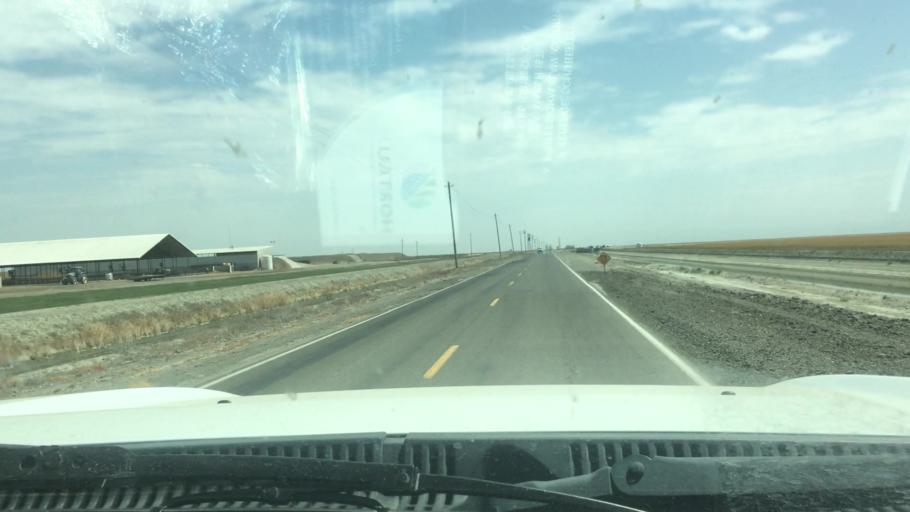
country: US
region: California
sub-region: Tulare County
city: Alpaugh
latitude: 35.9407
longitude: -119.5731
